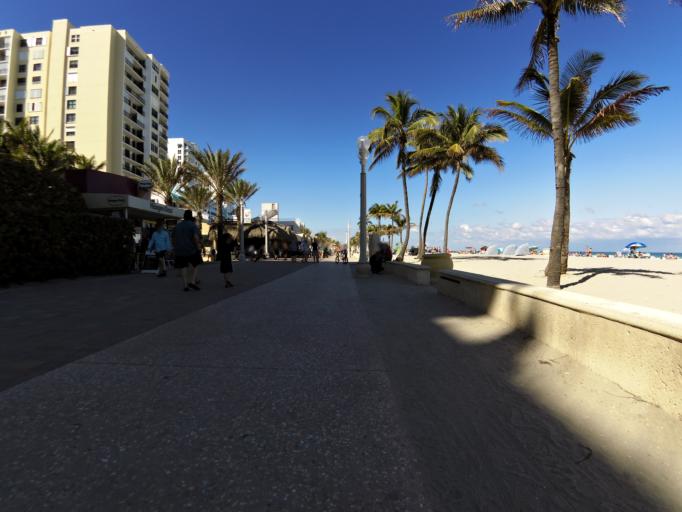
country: US
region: Florida
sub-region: Broward County
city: Hollywood
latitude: 26.0170
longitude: -80.1153
